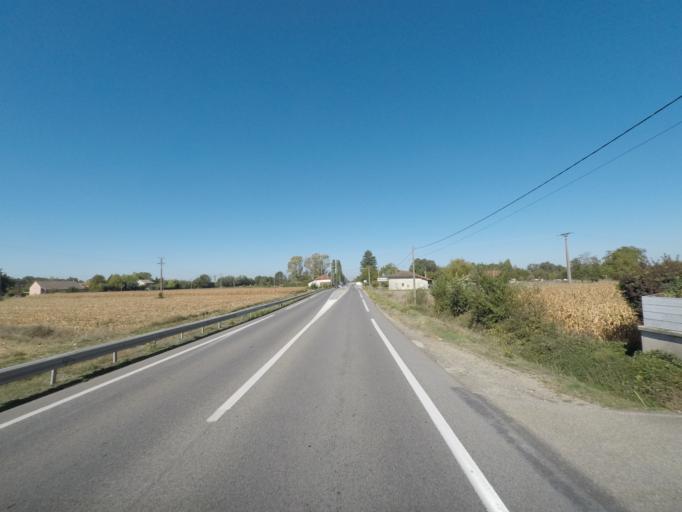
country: FR
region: Rhone-Alpes
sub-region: Departement de l'Ain
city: Viriat
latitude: 46.2466
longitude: 5.1879
